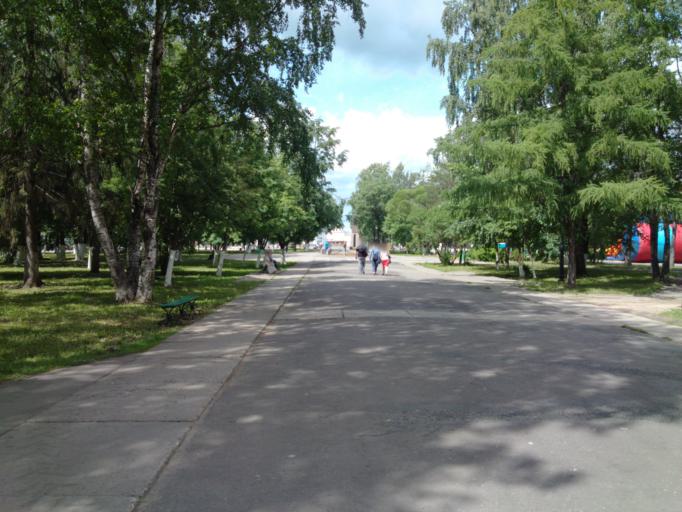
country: RU
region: Vologda
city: Vologda
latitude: 59.2178
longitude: 39.8956
